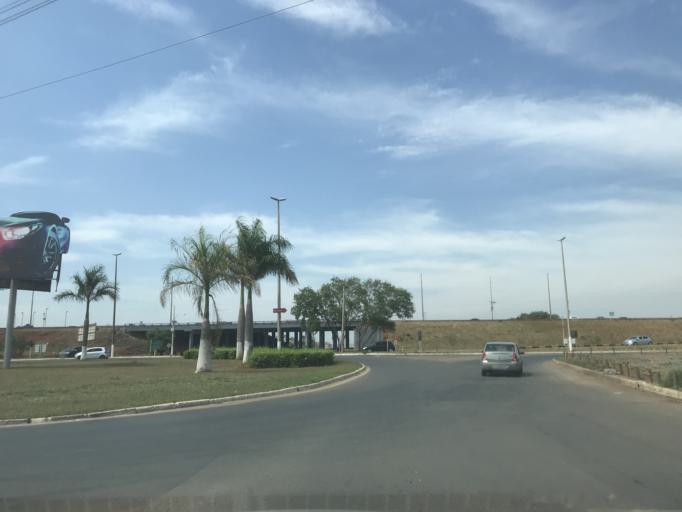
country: BR
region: Federal District
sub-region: Brasilia
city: Brasilia
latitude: -15.7940
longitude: -47.9698
